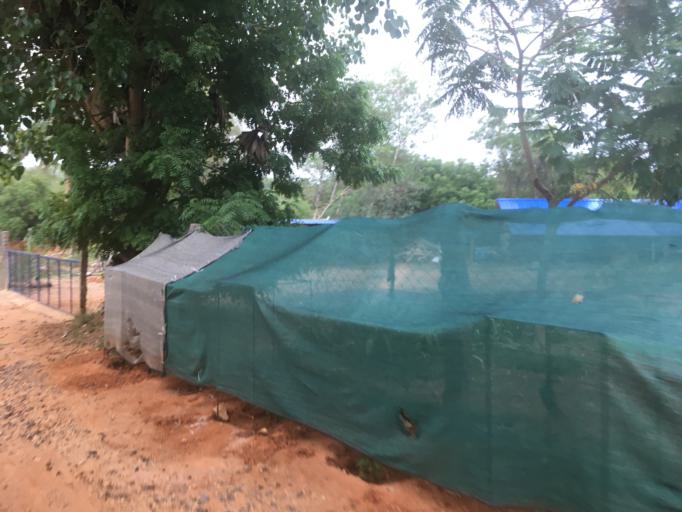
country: IN
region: Tamil Nadu
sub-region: Villupuram
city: Auroville
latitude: 12.0090
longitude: 79.8039
